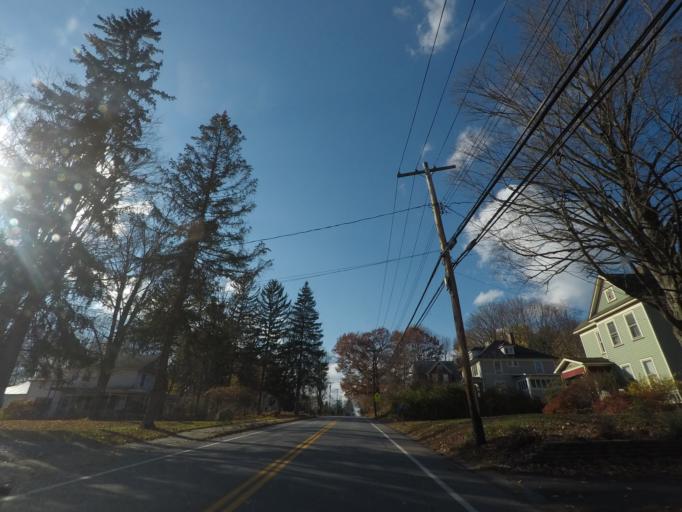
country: US
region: New York
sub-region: Schenectady County
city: East Glenville
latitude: 42.9111
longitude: -73.8785
